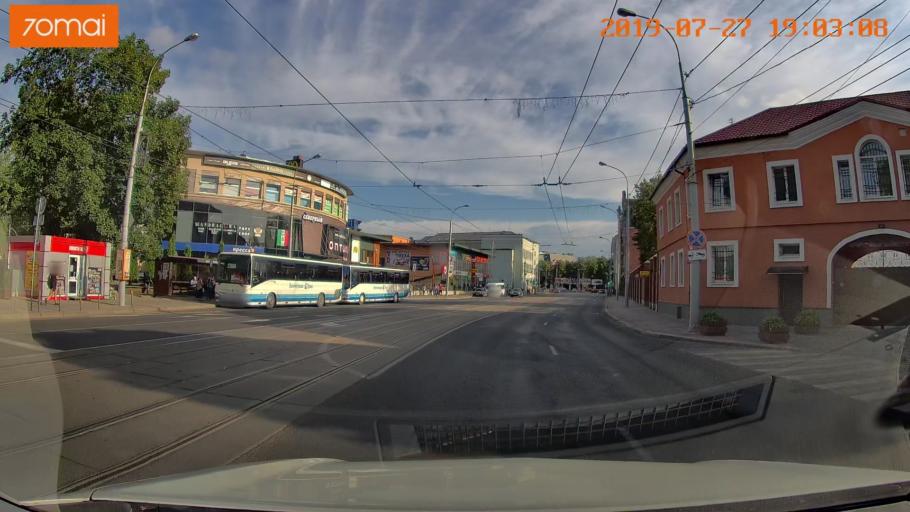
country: RU
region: Kaliningrad
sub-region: Gorod Kaliningrad
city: Kaliningrad
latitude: 54.7225
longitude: 20.4991
